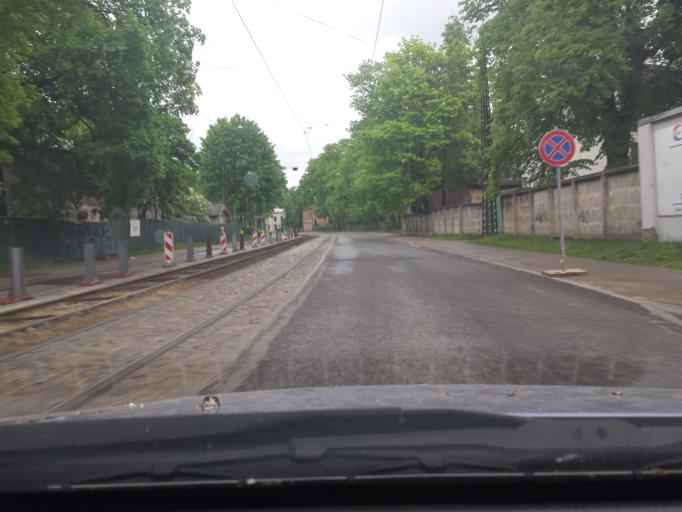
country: LV
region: Riga
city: Riga
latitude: 56.9544
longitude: 24.0631
